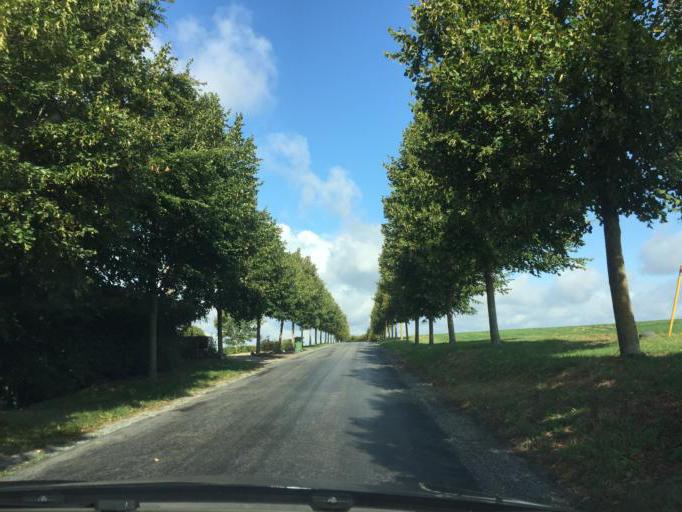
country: DK
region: South Denmark
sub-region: Faaborg-Midtfyn Kommune
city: Faaborg
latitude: 55.1954
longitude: 10.2743
